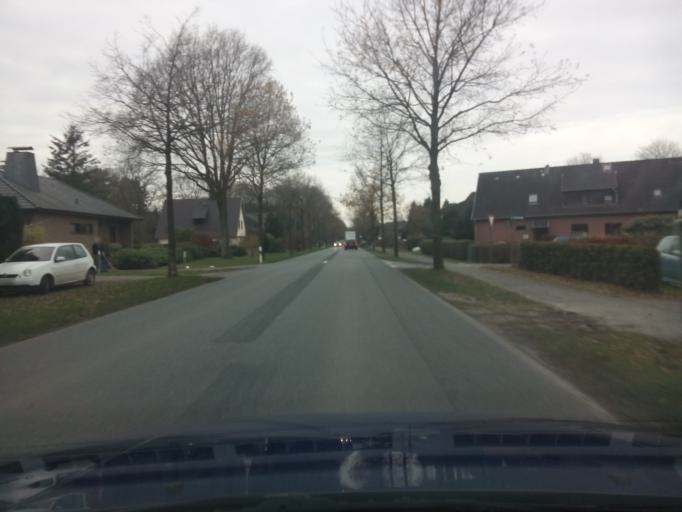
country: DE
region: Lower Saxony
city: Drangstedt
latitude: 53.6176
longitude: 8.7373
